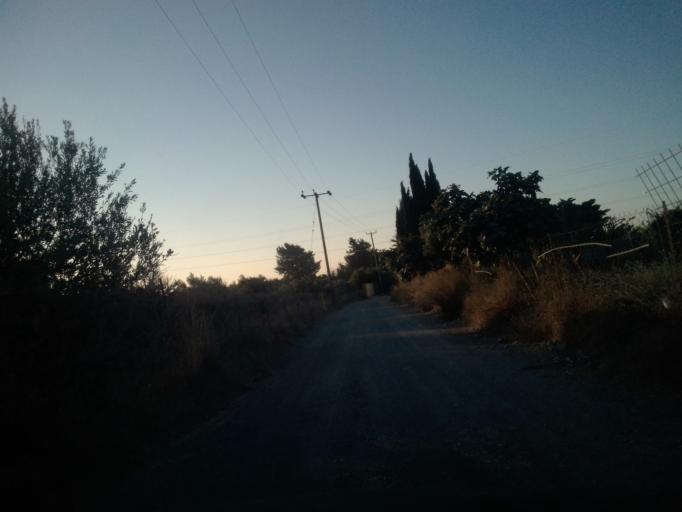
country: CY
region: Limassol
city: Ypsonas
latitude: 34.6685
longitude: 32.9675
